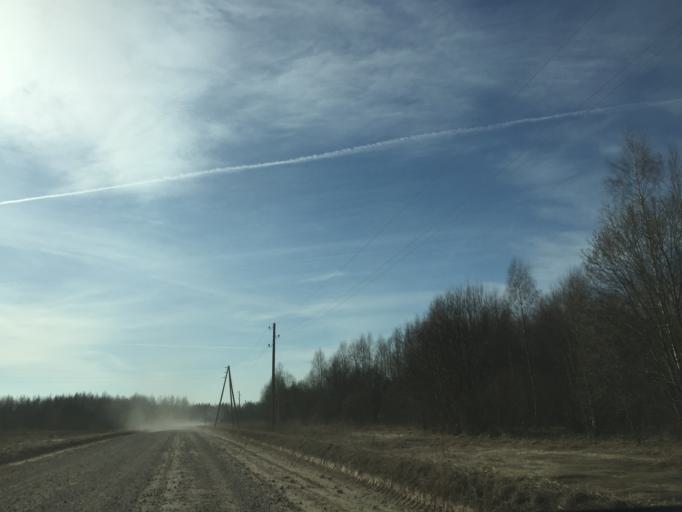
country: LV
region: Saulkrastu
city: Saulkrasti
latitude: 57.2849
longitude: 24.5011
